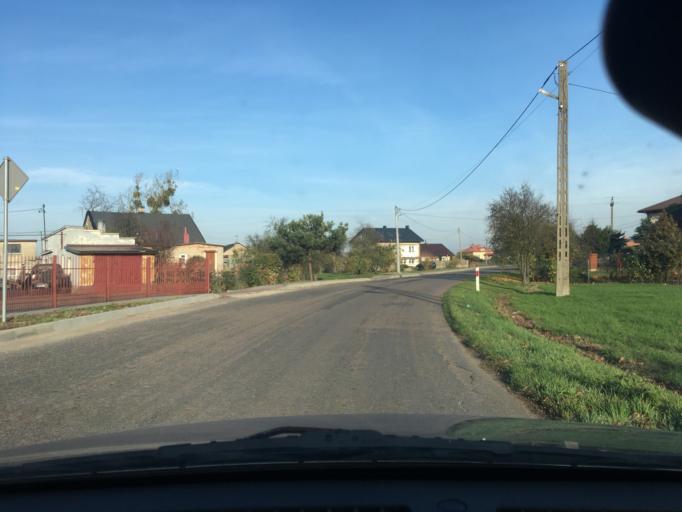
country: PL
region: Masovian Voivodeship
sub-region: Powiat plocki
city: Mala Wies
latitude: 52.4632
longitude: 20.1098
